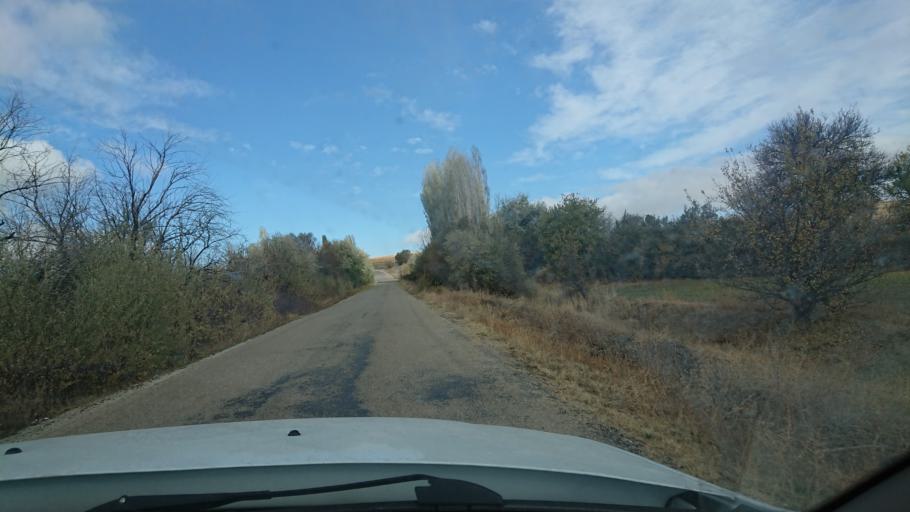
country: TR
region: Aksaray
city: Agacoren
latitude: 38.8314
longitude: 33.9559
